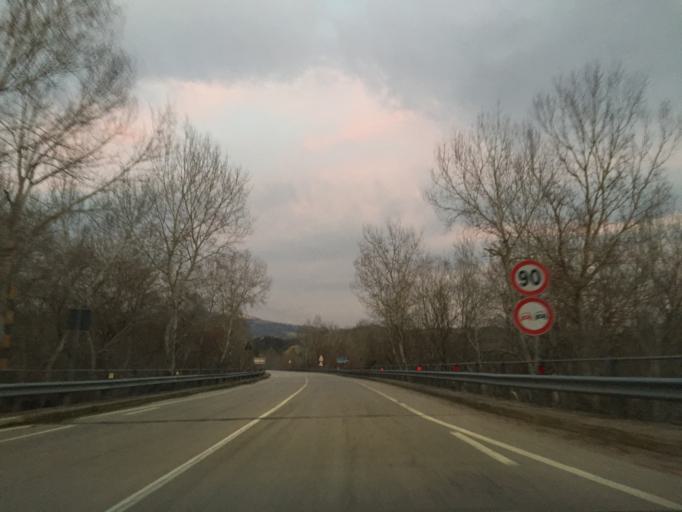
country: IT
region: Molise
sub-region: Provincia di Campobasso
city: Gambatesa
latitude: 41.5220
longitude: 14.9427
